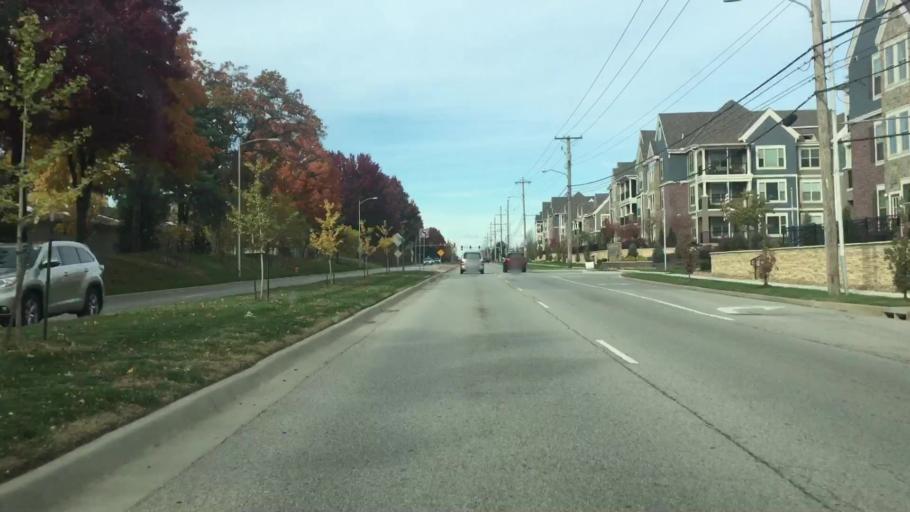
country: US
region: Kansas
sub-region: Johnson County
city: Lenexa
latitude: 38.9792
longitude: -94.7236
